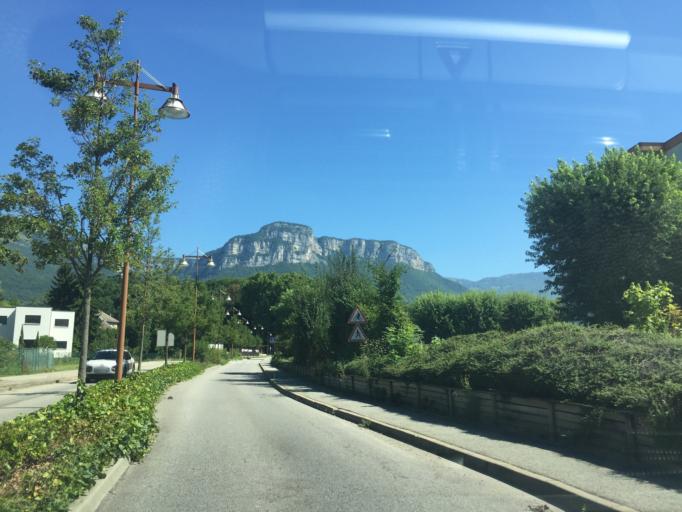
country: FR
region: Rhone-Alpes
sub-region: Departement de la Savoie
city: La Ravoire
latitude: 45.5606
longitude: 5.9604
